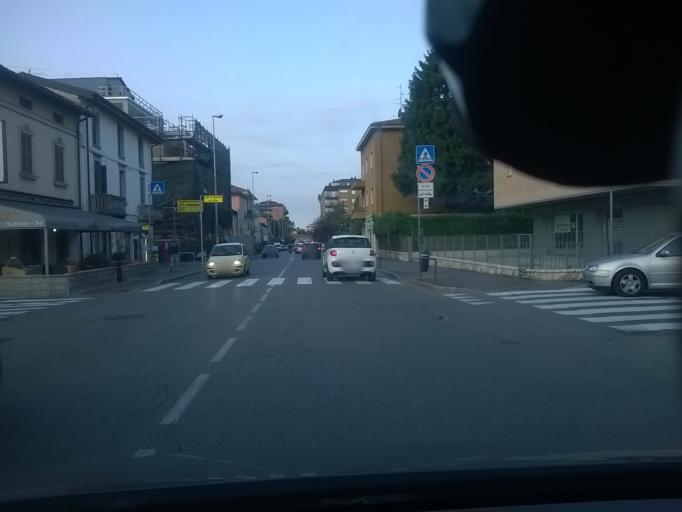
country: IT
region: Lombardy
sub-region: Provincia di Bergamo
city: Torre Boldone
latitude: 45.7105
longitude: 9.6968
